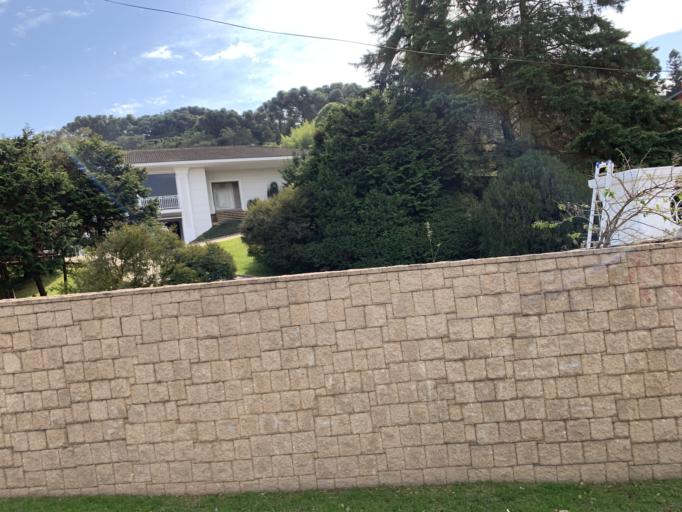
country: BR
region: Parana
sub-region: Curitiba
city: Curitiba
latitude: -25.3872
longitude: -49.3046
